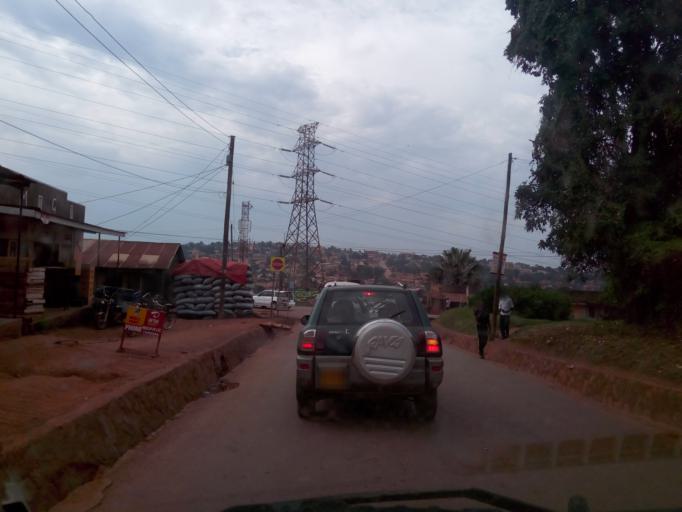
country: UG
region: Central Region
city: Kampala Central Division
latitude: 0.3468
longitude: 32.5779
